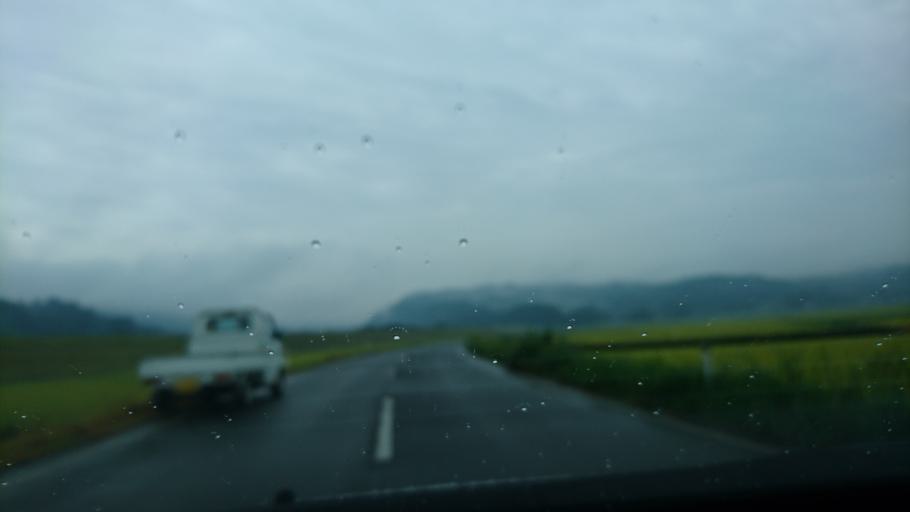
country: JP
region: Iwate
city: Ichinoseki
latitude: 38.8889
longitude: 141.2602
